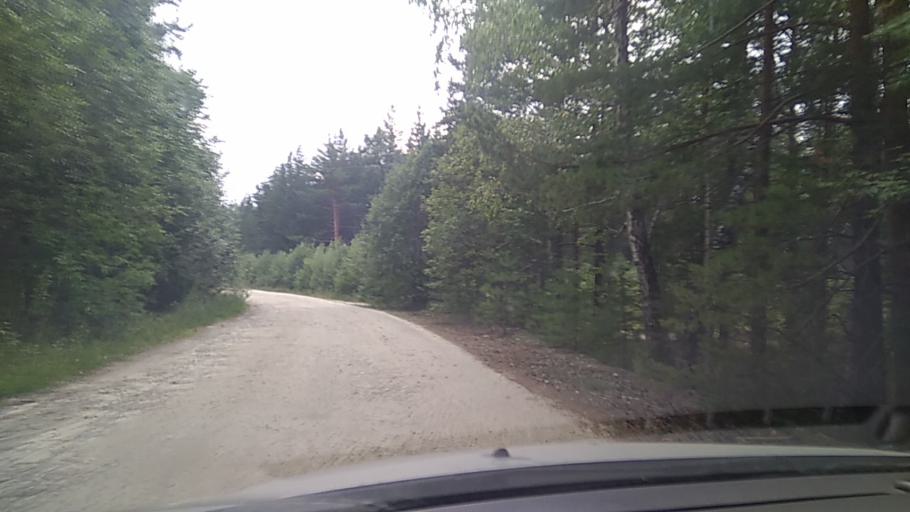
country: RU
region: Chelyabinsk
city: Kyshtym
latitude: 55.6795
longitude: 60.5795
